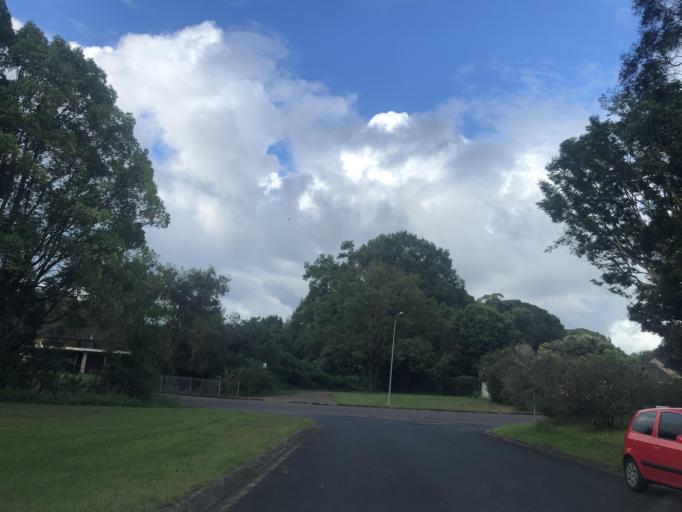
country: AU
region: New South Wales
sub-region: Bellingen
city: Bellingen
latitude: -30.4576
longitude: 152.9023
